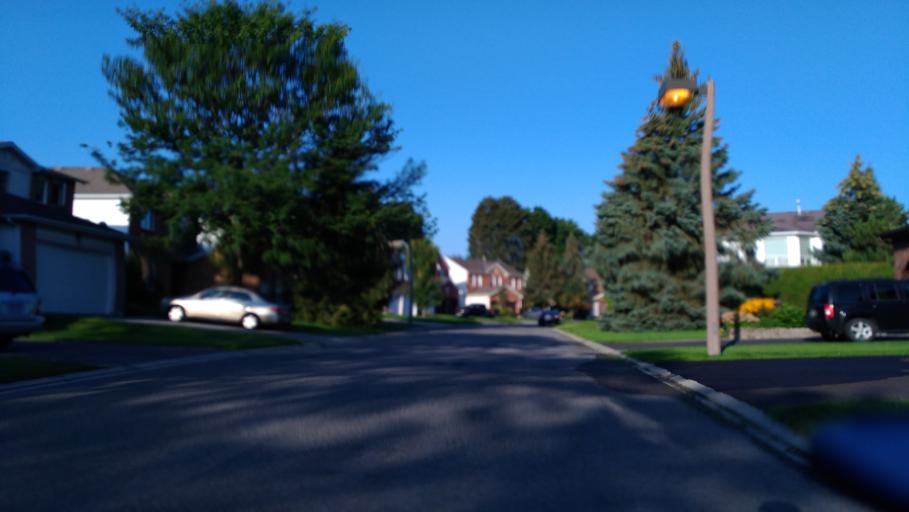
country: CA
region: Ontario
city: Bells Corners
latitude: 45.3468
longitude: -75.9338
